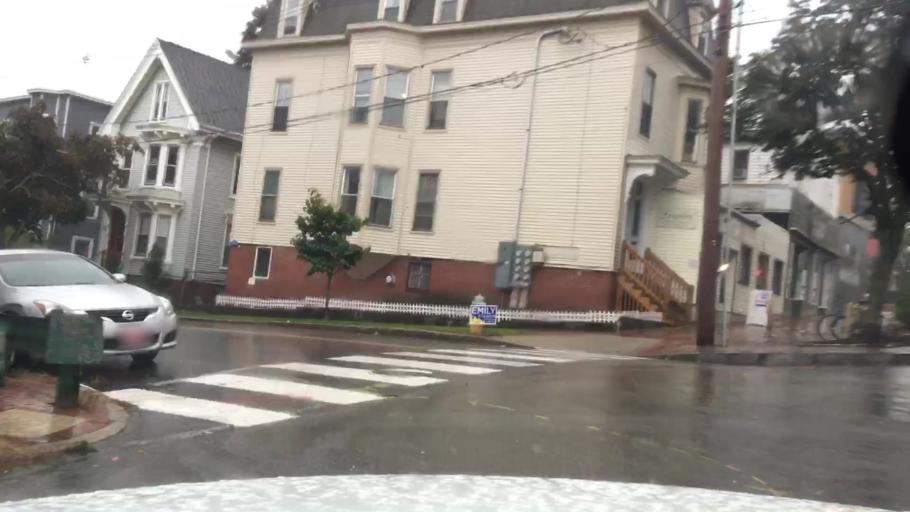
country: US
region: Maine
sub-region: Cumberland County
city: Portland
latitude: 43.6544
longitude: -70.2726
